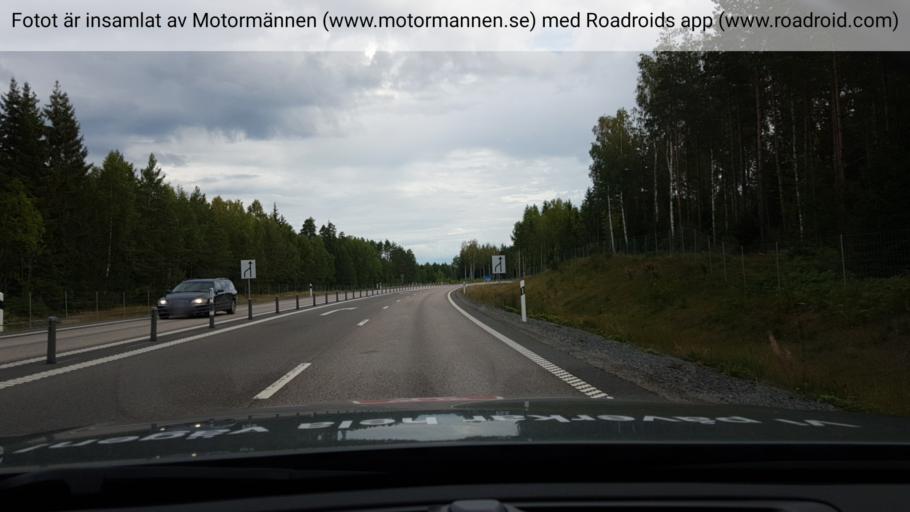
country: SE
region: Uppsala
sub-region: Heby Kommun
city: Heby
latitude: 59.9662
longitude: 16.8351
